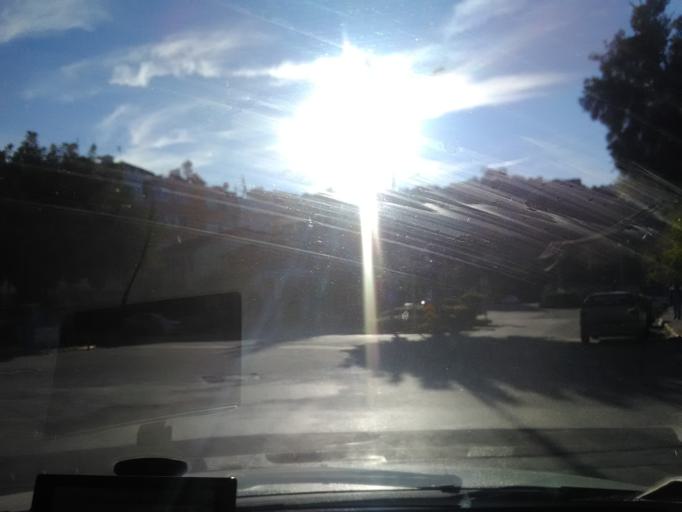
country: TR
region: Antalya
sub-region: Alanya
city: Alanya
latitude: 36.5436
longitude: 31.9881
